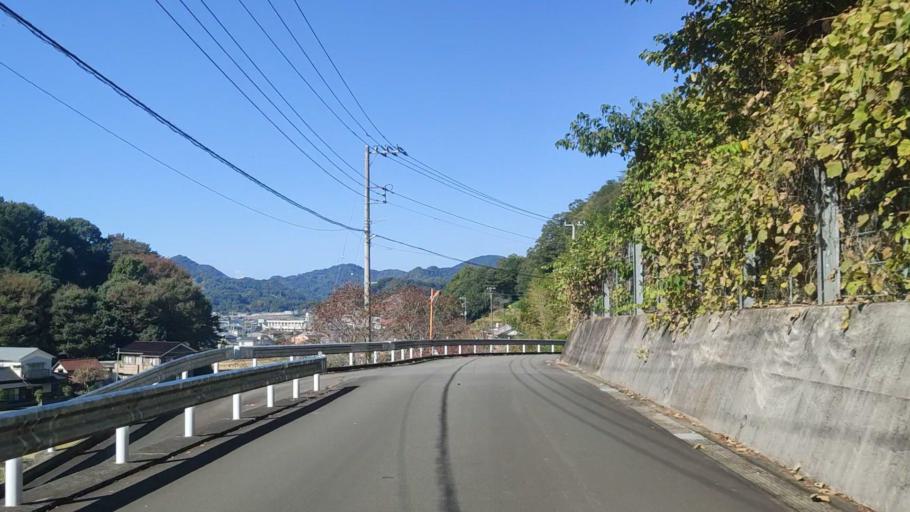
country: JP
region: Shizuoka
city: Mishima
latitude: 35.0163
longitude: 138.9551
